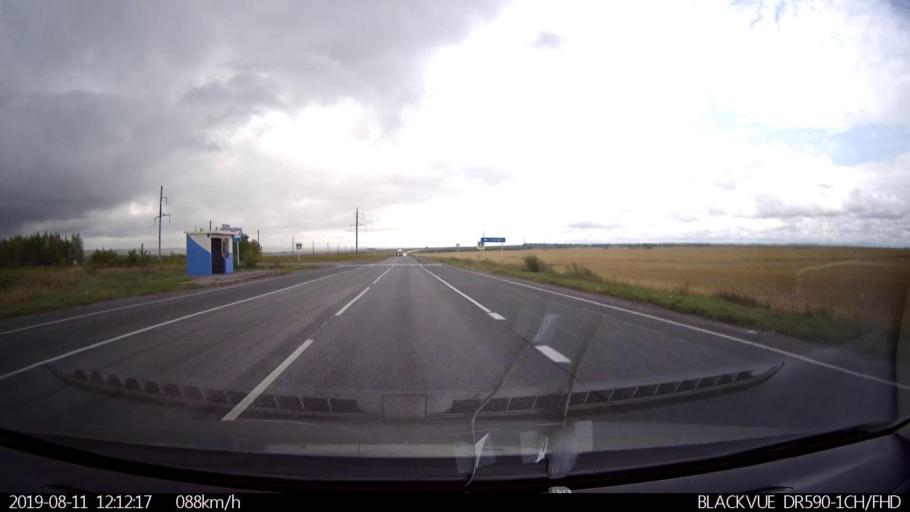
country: RU
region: Ulyanovsk
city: Silikatnyy
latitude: 53.9752
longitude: 47.9974
